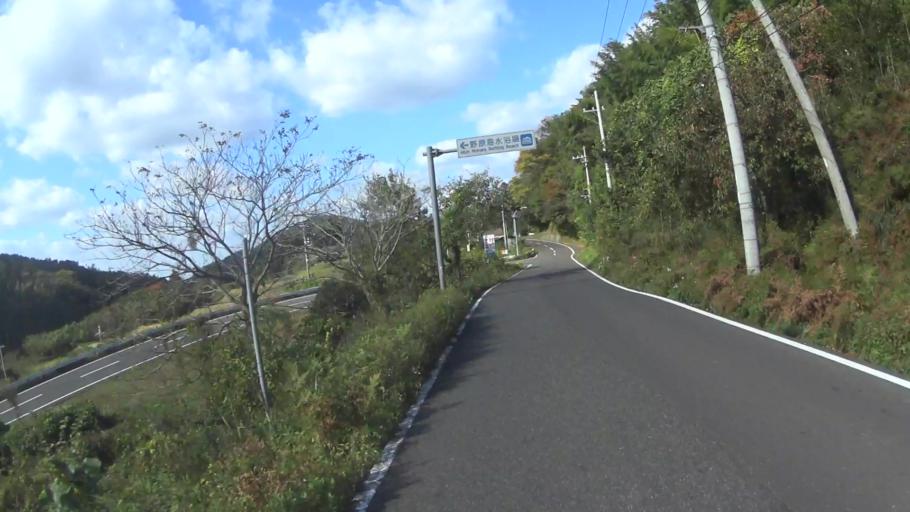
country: JP
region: Kyoto
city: Maizuru
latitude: 35.5467
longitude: 135.4519
